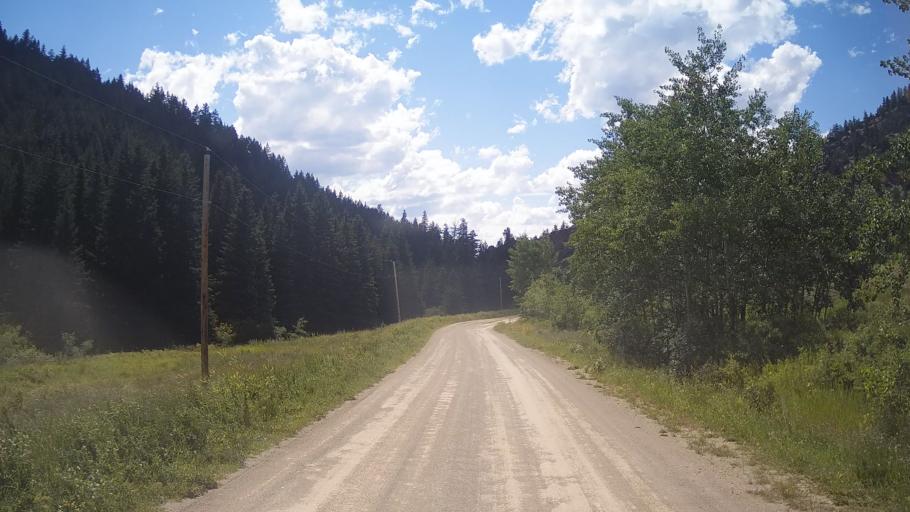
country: CA
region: British Columbia
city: Lillooet
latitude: 51.2549
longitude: -122.0064
